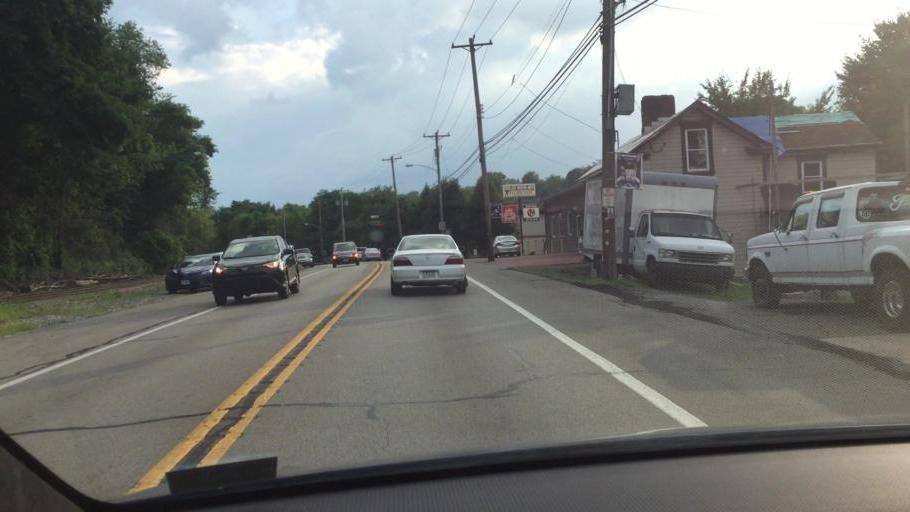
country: US
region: Pennsylvania
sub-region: Allegheny County
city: Castle Shannon
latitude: 40.3641
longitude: -80.0254
